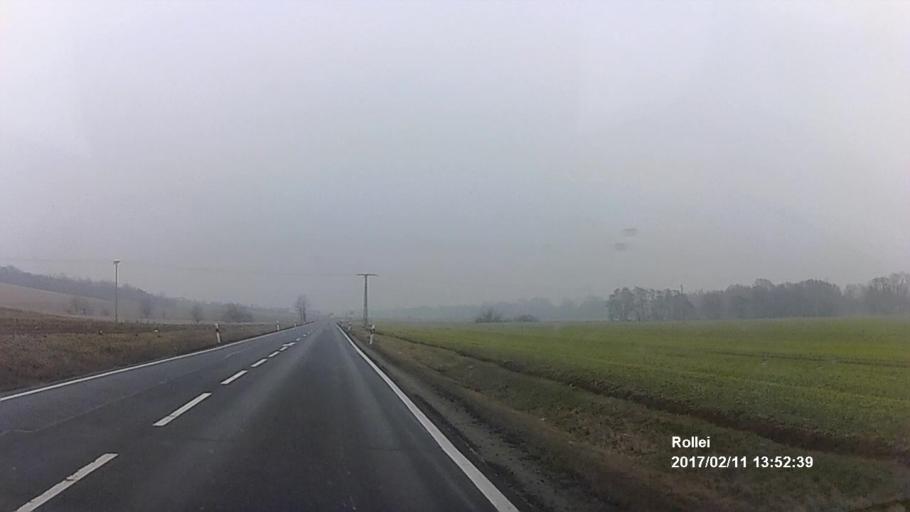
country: DE
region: Thuringia
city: Wipperdorf
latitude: 51.5145
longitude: 10.6846
